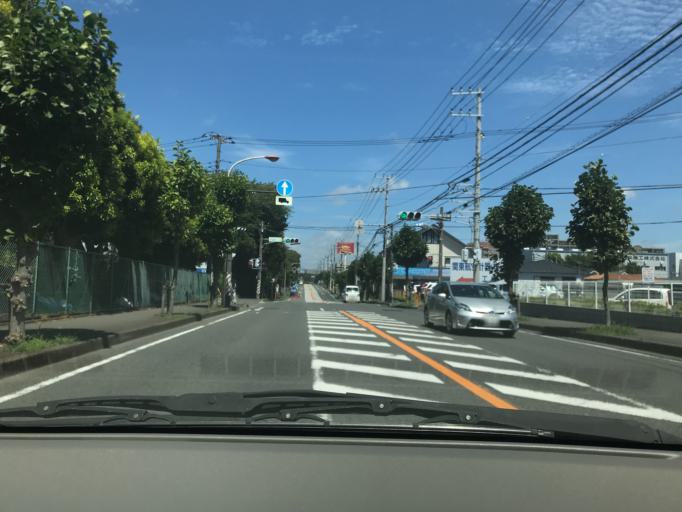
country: JP
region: Kanagawa
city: Fujisawa
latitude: 35.3551
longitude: 139.4675
